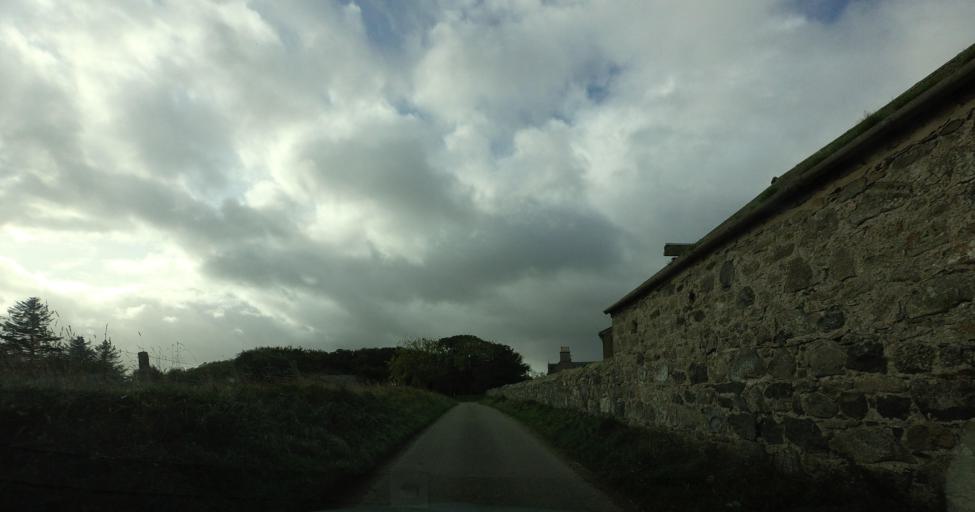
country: GB
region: Scotland
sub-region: Aberdeenshire
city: Whitehills
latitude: 57.6648
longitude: -2.5997
